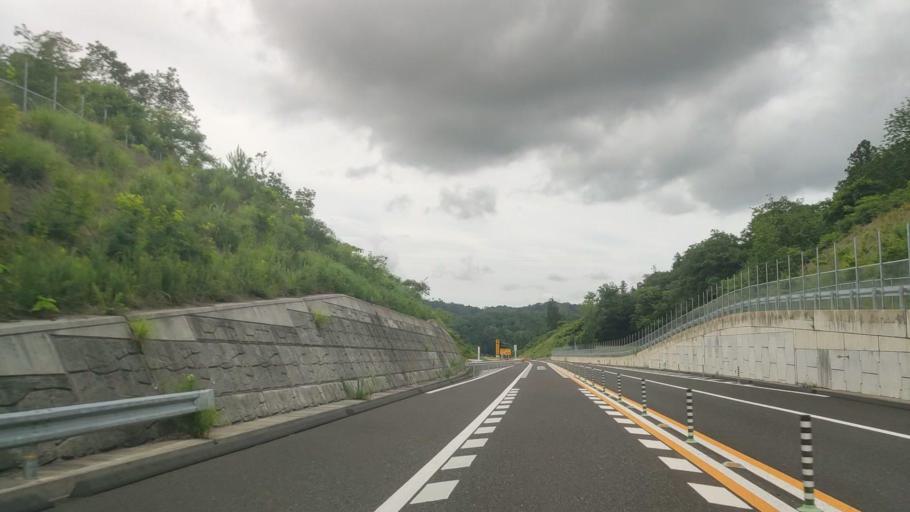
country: JP
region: Kyoto
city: Miyazu
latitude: 35.5716
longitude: 135.1211
